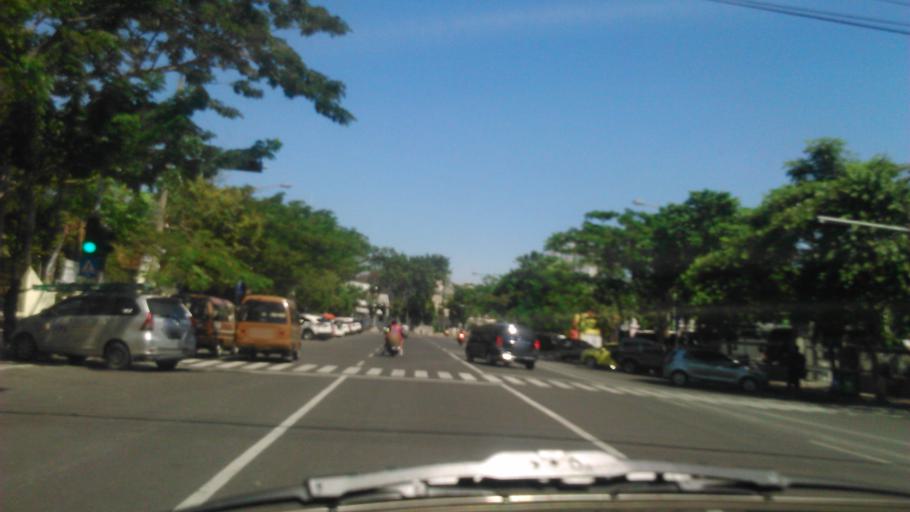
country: ID
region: East Java
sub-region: Kota Surabaya
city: Surabaya
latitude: -7.2569
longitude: 112.7489
